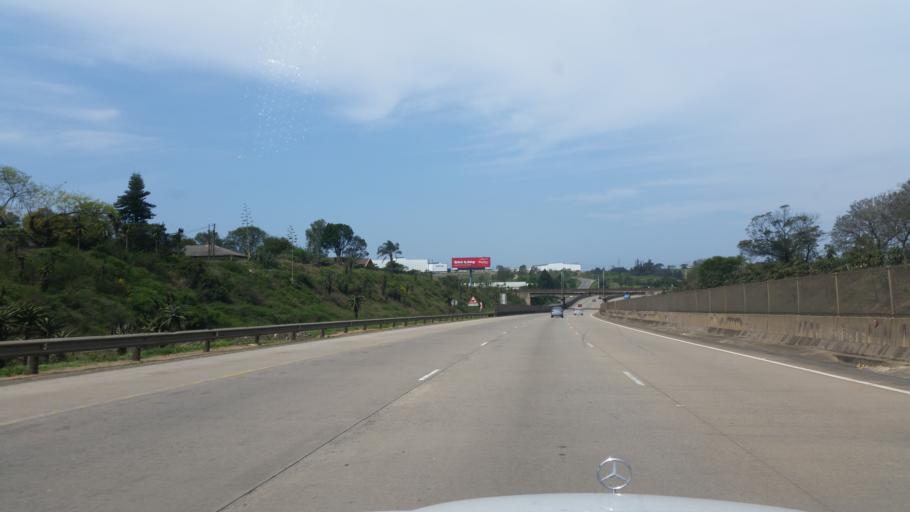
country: ZA
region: KwaZulu-Natal
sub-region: uMgungundlovu District Municipality
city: Camperdown
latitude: -29.7323
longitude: 30.5921
